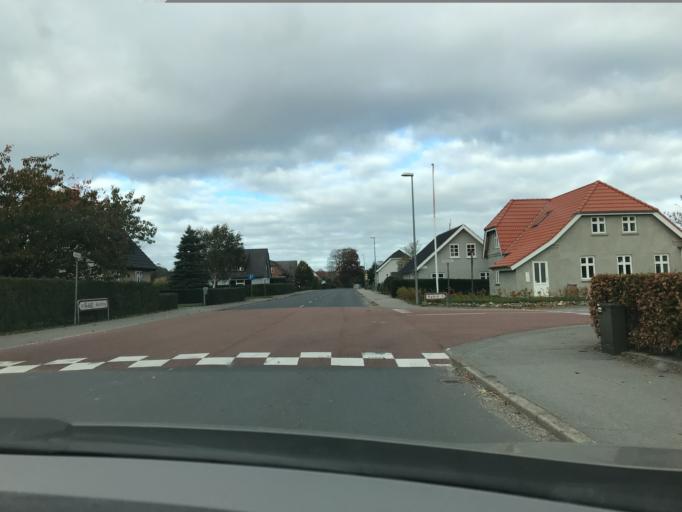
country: DK
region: South Denmark
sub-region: Kolding Kommune
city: Kolding
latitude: 55.5655
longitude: 9.4039
